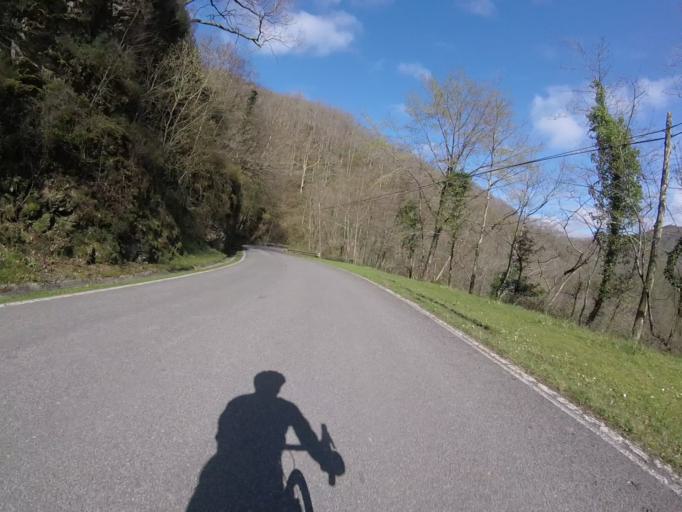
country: ES
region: Navarre
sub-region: Provincia de Navarra
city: Goizueta
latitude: 43.1348
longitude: -1.8501
